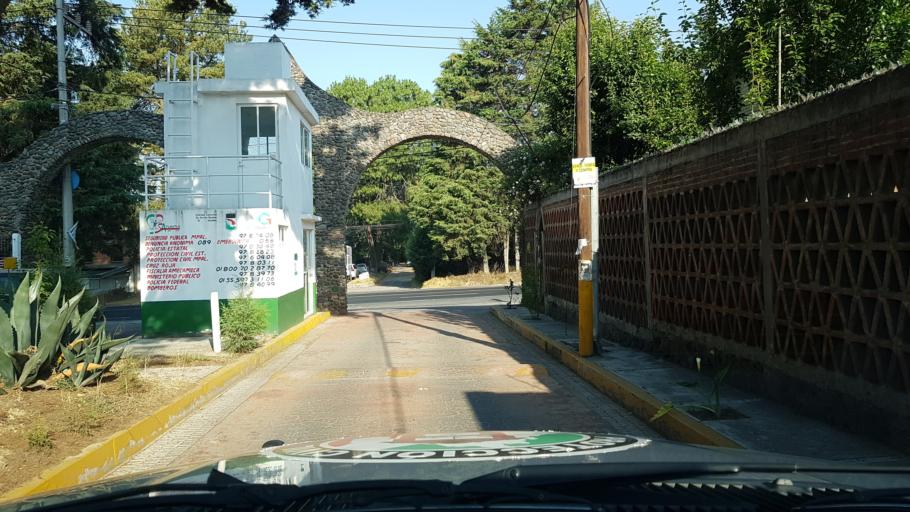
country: MX
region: Mexico
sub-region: Amecameca
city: San Diego Huehuecalco
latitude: 19.0733
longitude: -98.7809
